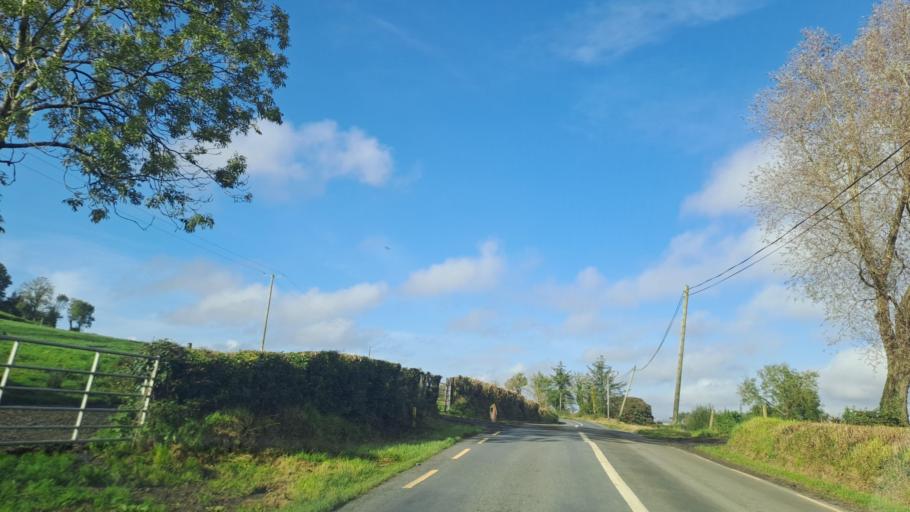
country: IE
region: Ulster
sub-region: An Cabhan
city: Cootehill
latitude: 54.0653
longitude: -7.0509
